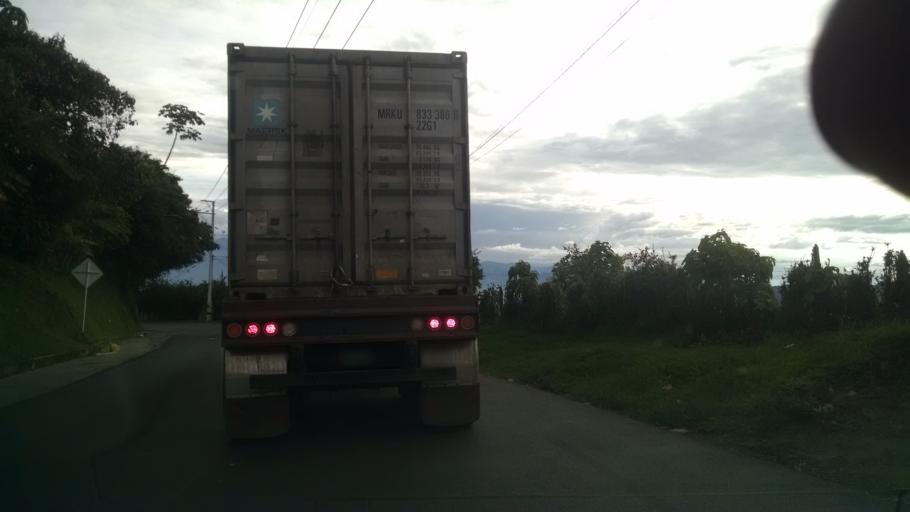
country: CO
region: Antioquia
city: Santa Barbara
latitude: 5.9211
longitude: -75.5785
